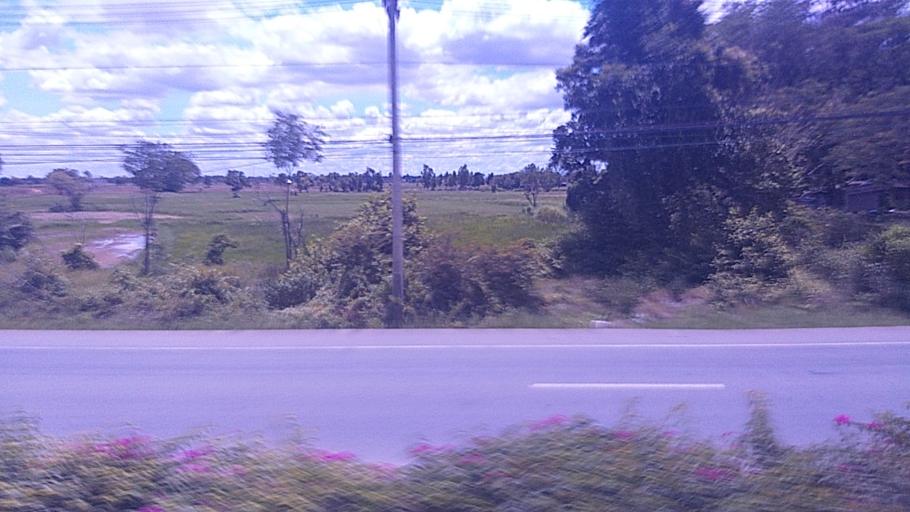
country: TH
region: Chaiyaphum
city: Noen Sa-nga
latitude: 15.6791
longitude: 102.0083
